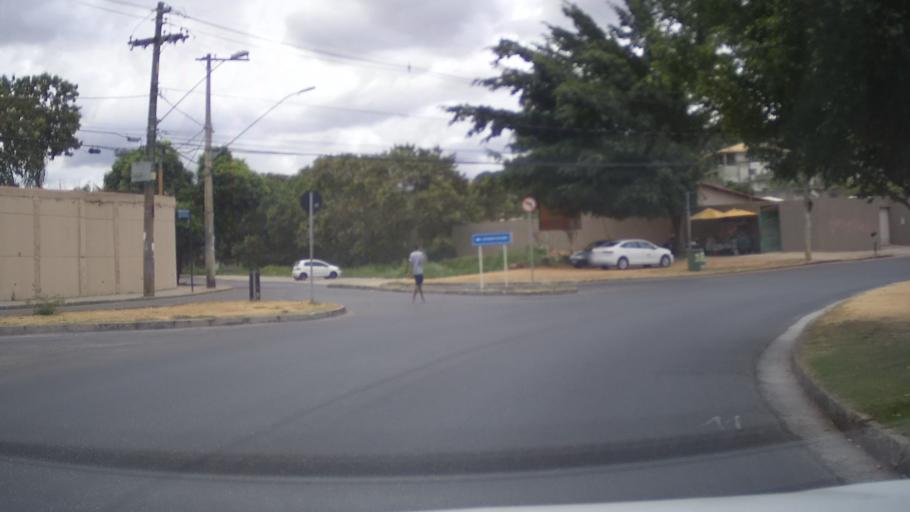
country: BR
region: Minas Gerais
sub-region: Belo Horizonte
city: Belo Horizonte
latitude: -19.8384
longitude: -43.9948
